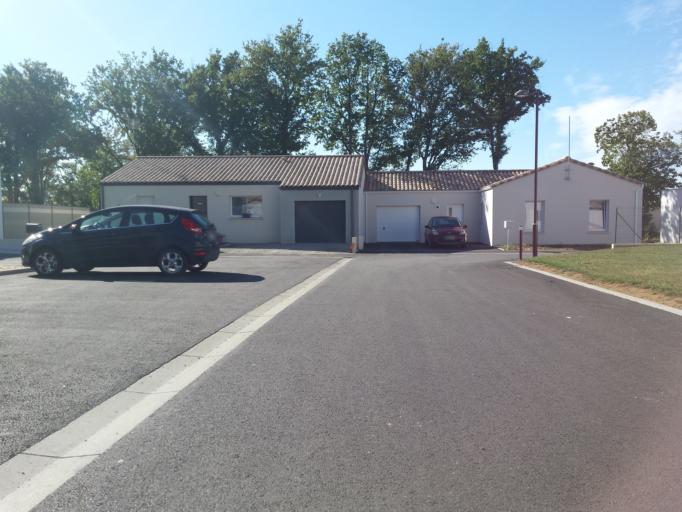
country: FR
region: Pays de la Loire
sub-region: Departement de la Vendee
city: La Ferriere
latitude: 46.7115
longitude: -1.3238
